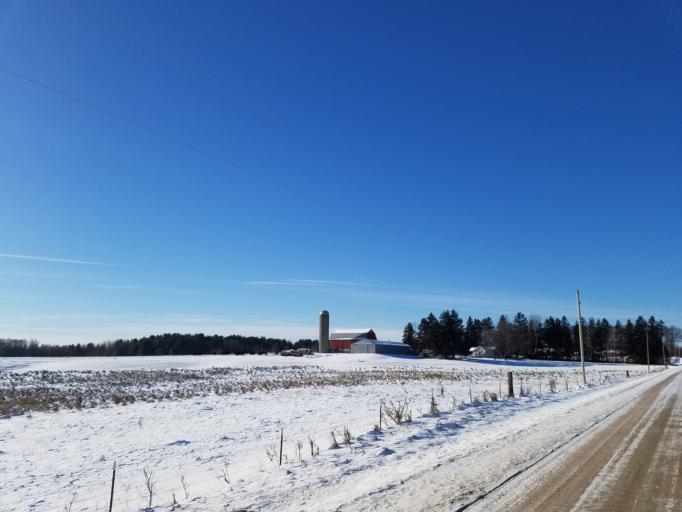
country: US
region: Wisconsin
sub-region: Clark County
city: Loyal
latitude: 44.6259
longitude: -90.4033
